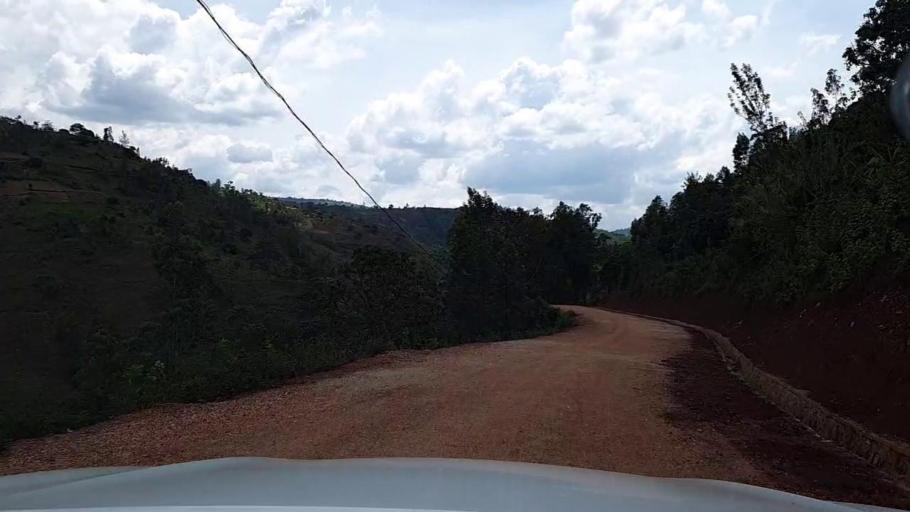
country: BI
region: Ngozi
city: Ngozi
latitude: -2.8101
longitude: 29.7318
